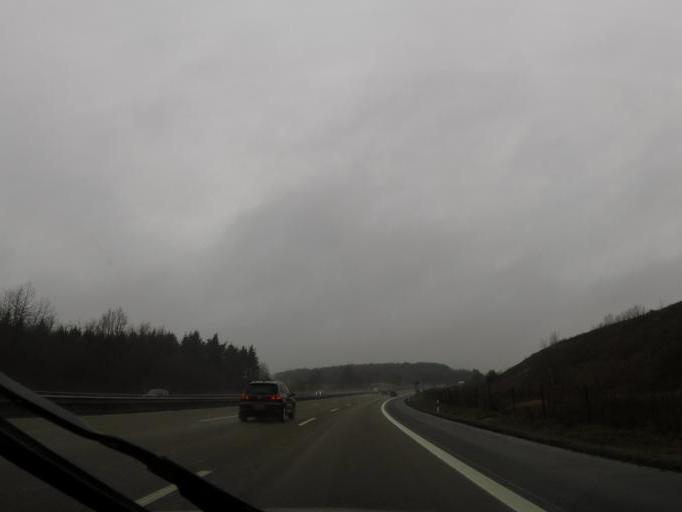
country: DE
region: Rheinland-Pfalz
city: Eppenrod
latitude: 50.4161
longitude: 7.9298
